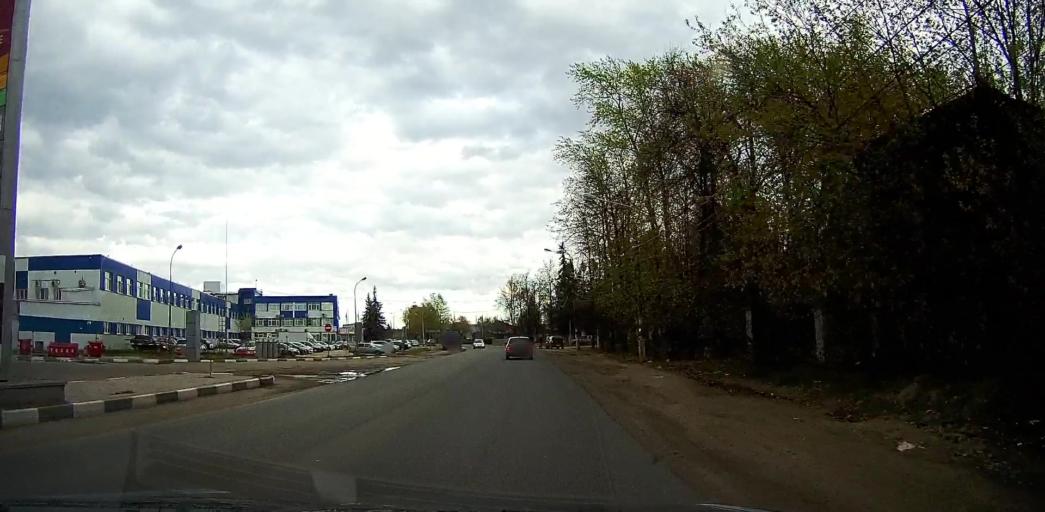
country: RU
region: Moskovskaya
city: Pavlovskiy Posad
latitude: 55.7728
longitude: 38.6870
